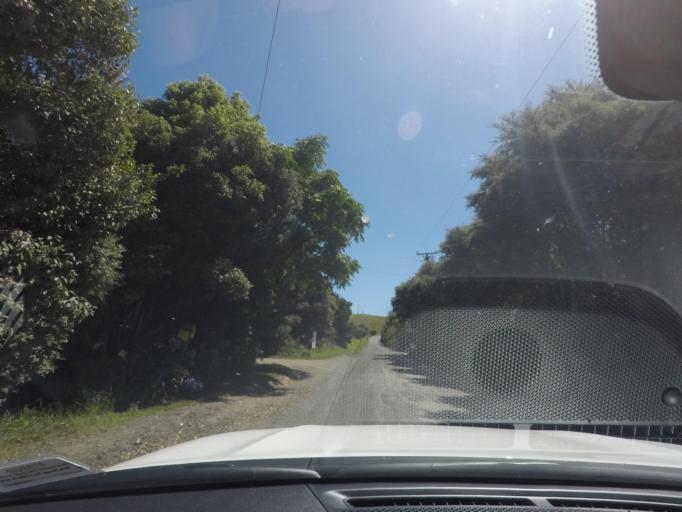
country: NZ
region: Auckland
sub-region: Auckland
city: Parakai
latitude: -36.5815
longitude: 174.3143
